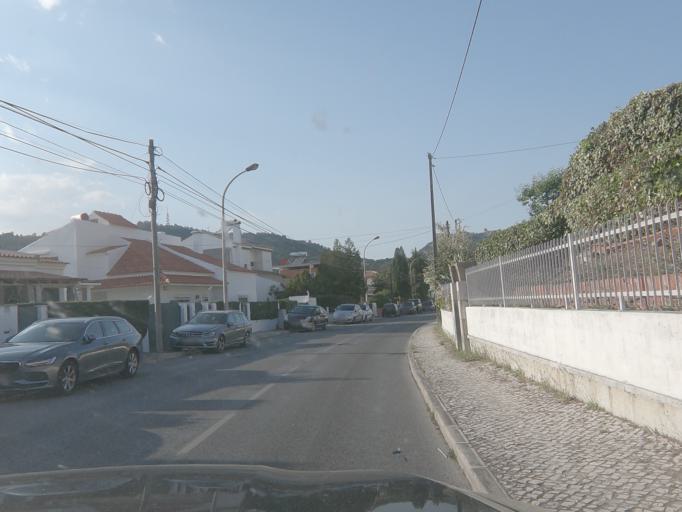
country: PT
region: Setubal
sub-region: Setubal
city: Setubal
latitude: 38.5451
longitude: -8.8990
